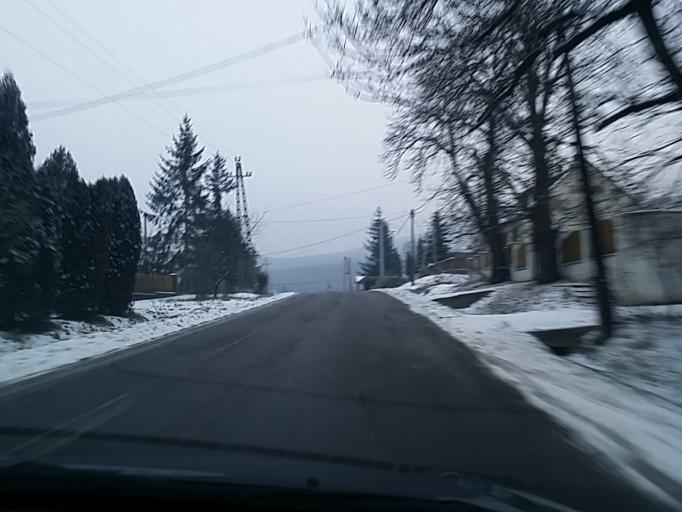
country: HU
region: Heves
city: Sirok
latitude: 47.9020
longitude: 20.1792
